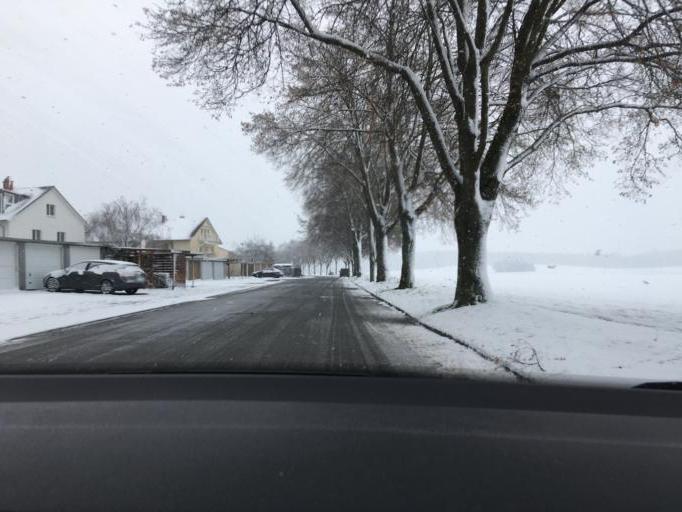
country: DE
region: Baden-Wuerttemberg
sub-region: Freiburg Region
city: Gottmadingen
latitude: 47.7314
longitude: 8.7861
